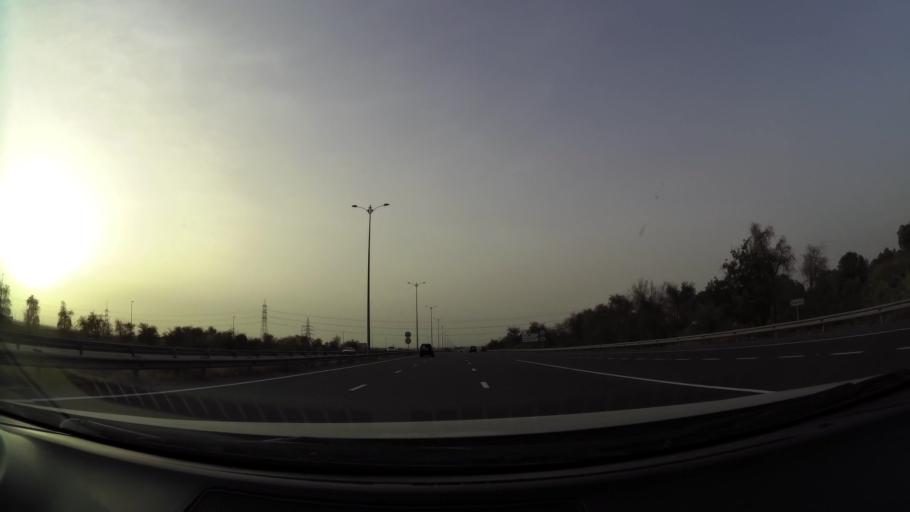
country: OM
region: Al Buraimi
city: Al Buraymi
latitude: 24.3903
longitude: 55.7981
